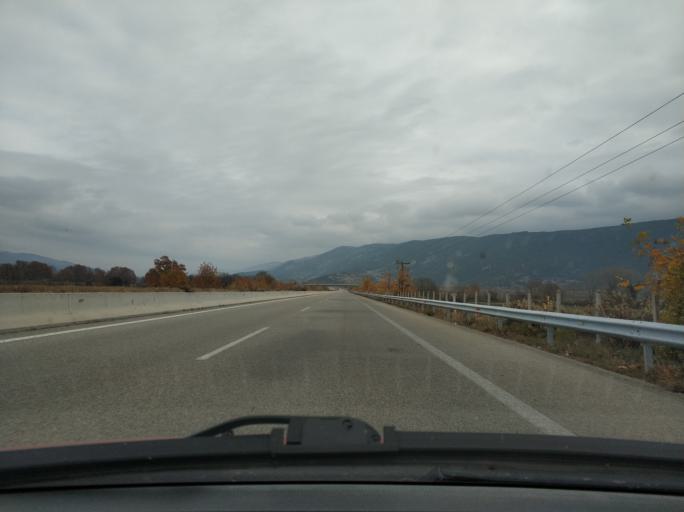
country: GR
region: Central Macedonia
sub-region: Nomos Serron
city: Rodolivos
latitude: 40.8231
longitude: 24.0732
